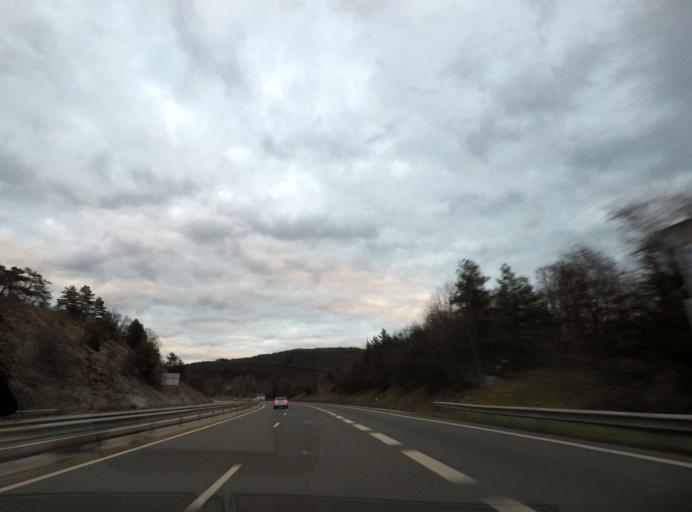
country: FR
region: Rhone-Alpes
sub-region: Departement de l'Ain
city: Saint-Martin-du-Frene
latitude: 46.1123
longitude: 5.4811
